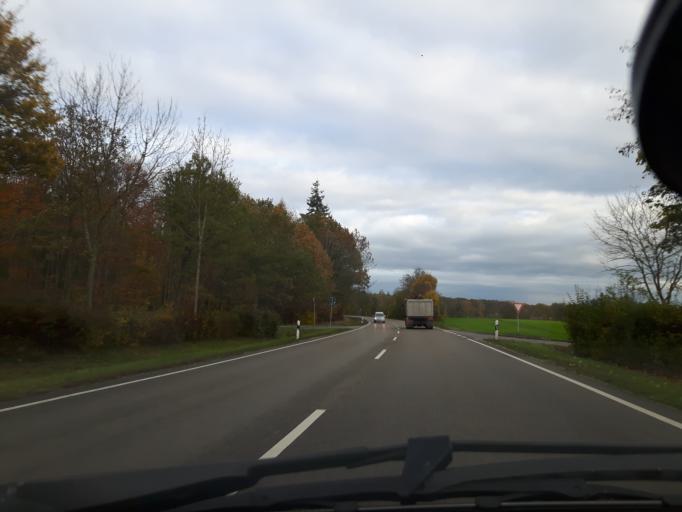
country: DE
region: Bavaria
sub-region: Regierungsbezirk Mittelfranken
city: Weidenbach
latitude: 49.2114
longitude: 10.6496
